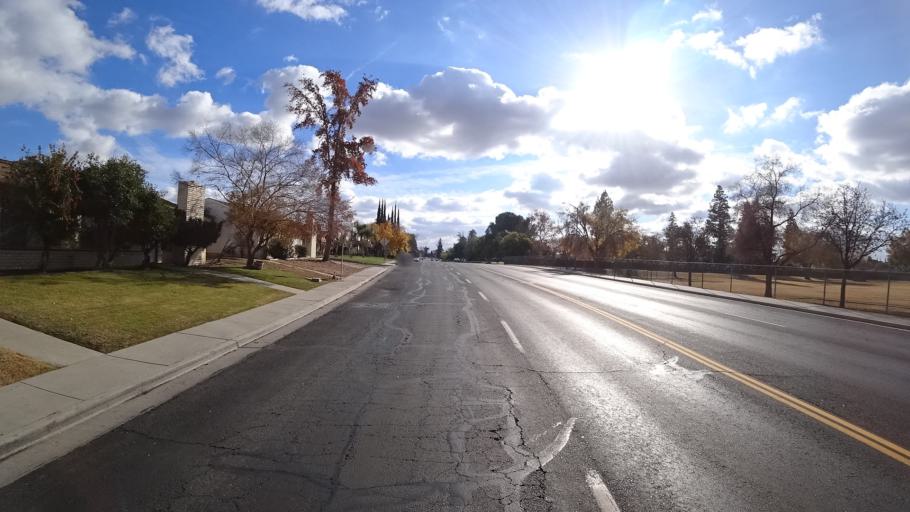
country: US
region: California
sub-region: Kern County
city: Bakersfield
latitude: 35.3291
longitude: -119.0657
